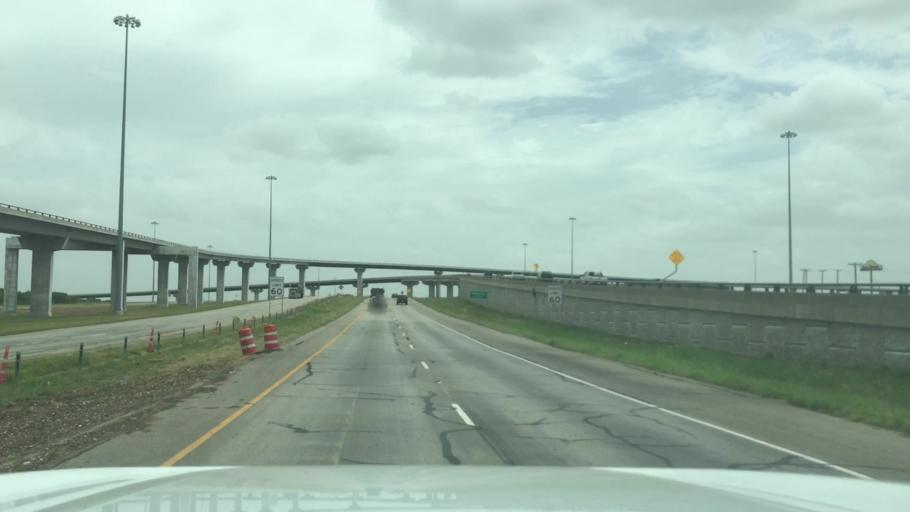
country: US
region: Texas
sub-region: McLennan County
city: Beverly Hills
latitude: 31.4954
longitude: -97.1562
